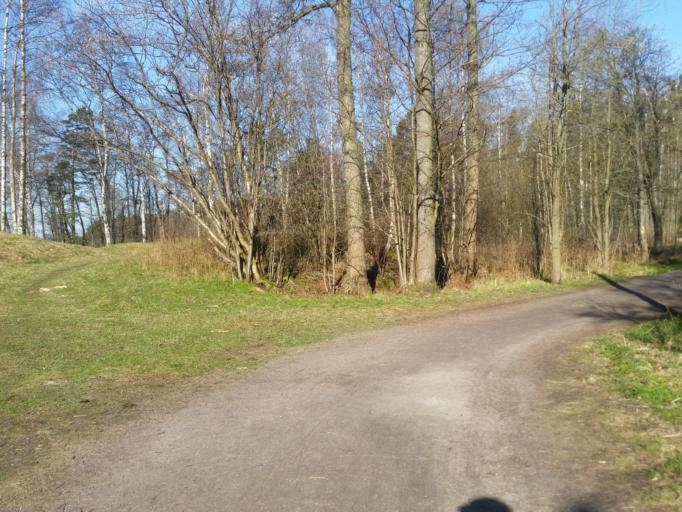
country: FI
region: Uusimaa
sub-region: Helsinki
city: Helsinki
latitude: 60.1459
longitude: 24.8861
